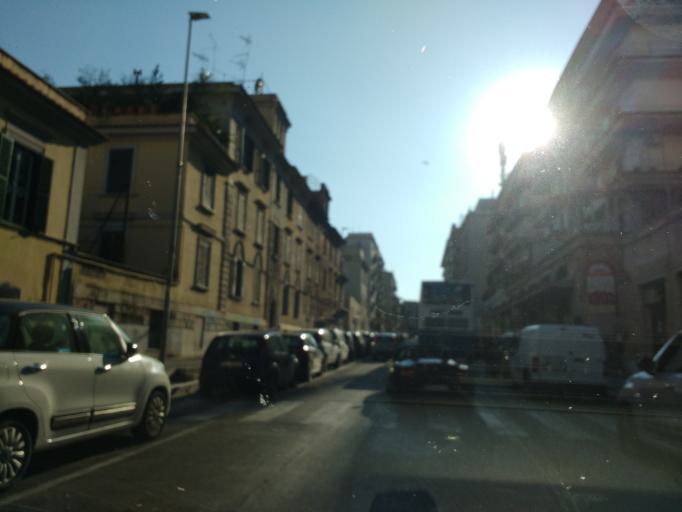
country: IT
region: Latium
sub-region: Citta metropolitana di Roma Capitale
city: Tivoli
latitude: 41.9598
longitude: 12.8013
